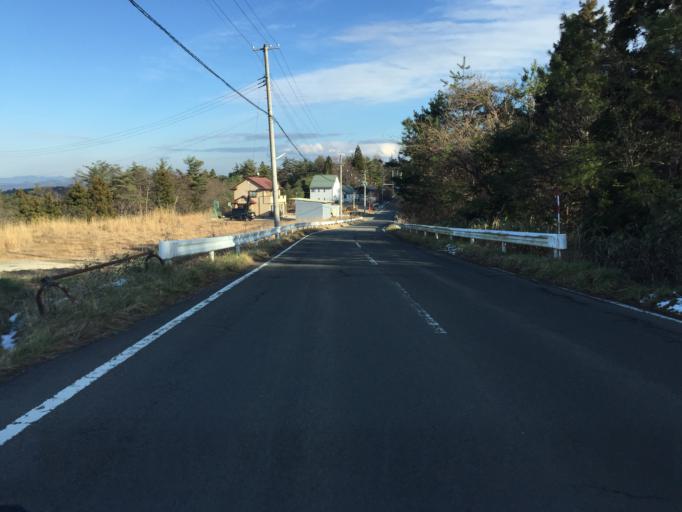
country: JP
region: Fukushima
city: Fukushima-shi
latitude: 37.7037
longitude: 140.3732
